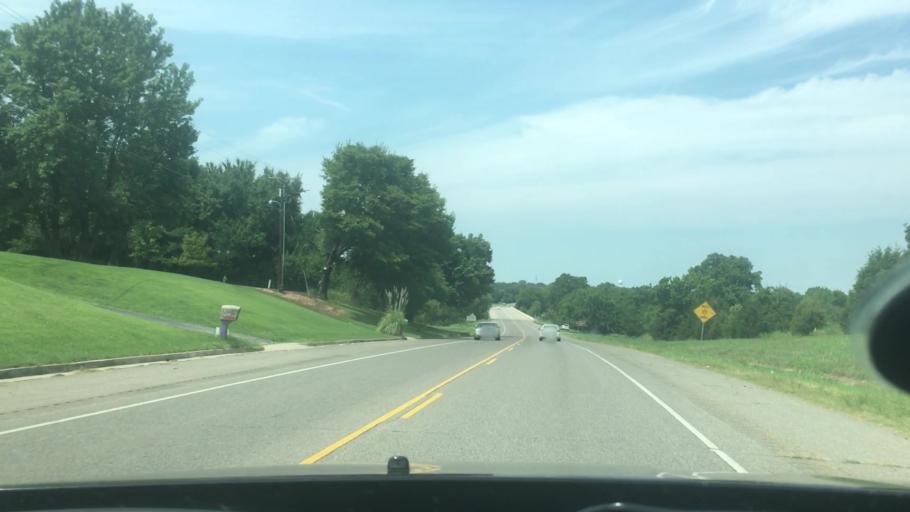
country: US
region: Oklahoma
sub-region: Pottawatomie County
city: Shawnee
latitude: 35.3332
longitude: -96.8655
